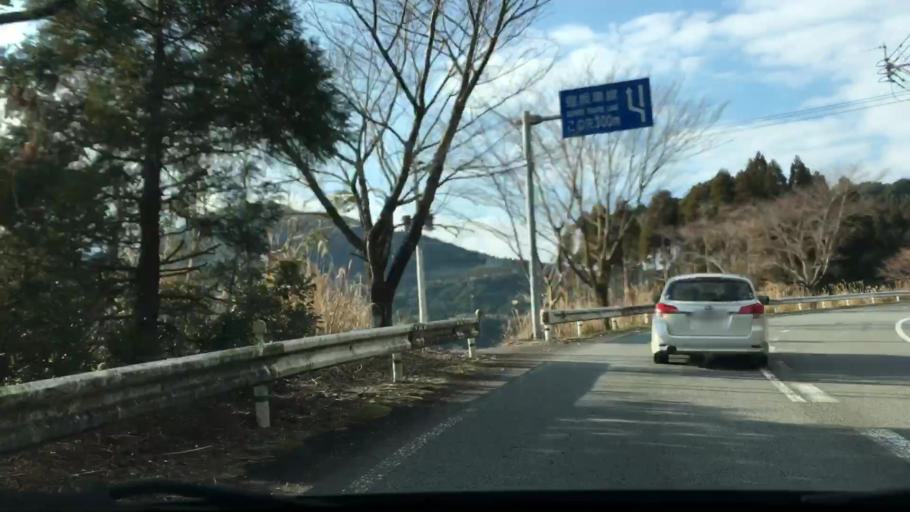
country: JP
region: Miyazaki
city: Miyazaki-shi
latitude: 31.7770
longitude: 131.3308
